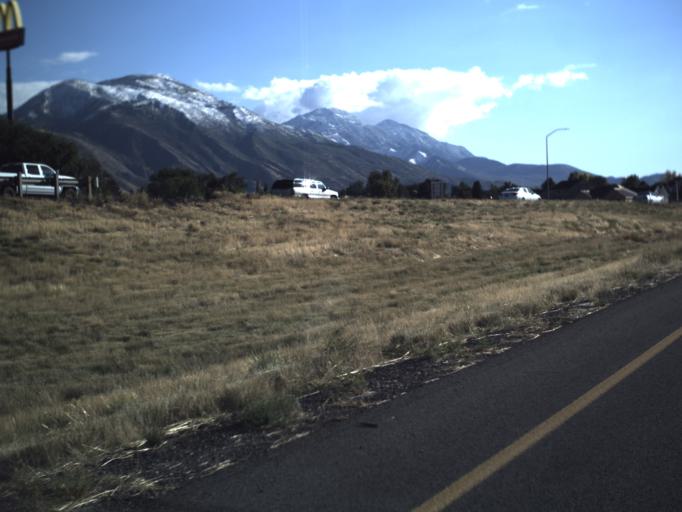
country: US
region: Utah
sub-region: Utah County
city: Payson
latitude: 40.0550
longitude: -111.7337
